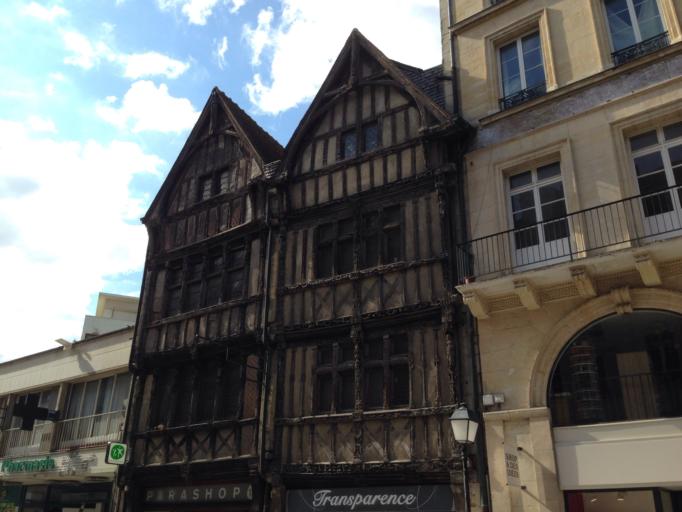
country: FR
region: Lower Normandy
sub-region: Departement du Calvados
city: Caen
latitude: 49.1835
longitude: -0.3633
